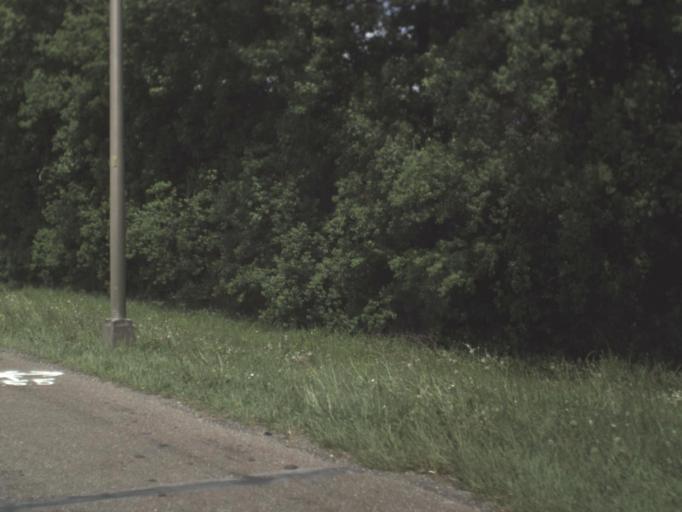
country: US
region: Florida
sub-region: Duval County
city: Jacksonville
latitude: 30.3567
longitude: -81.7607
